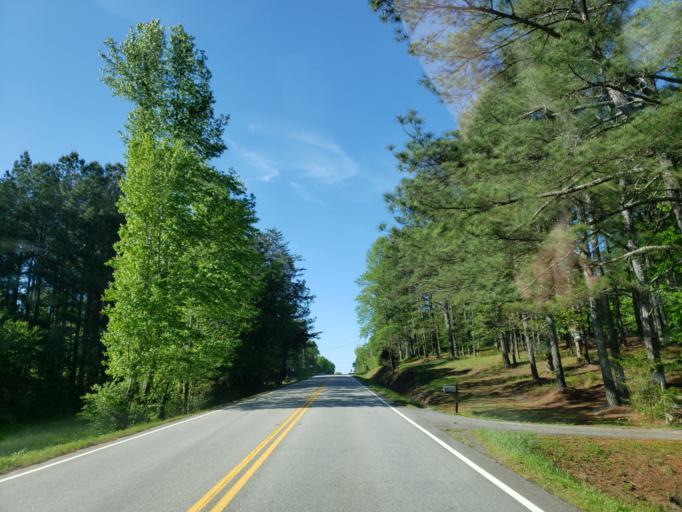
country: US
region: Georgia
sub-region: Haralson County
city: Tallapoosa
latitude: 33.8994
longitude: -85.3124
